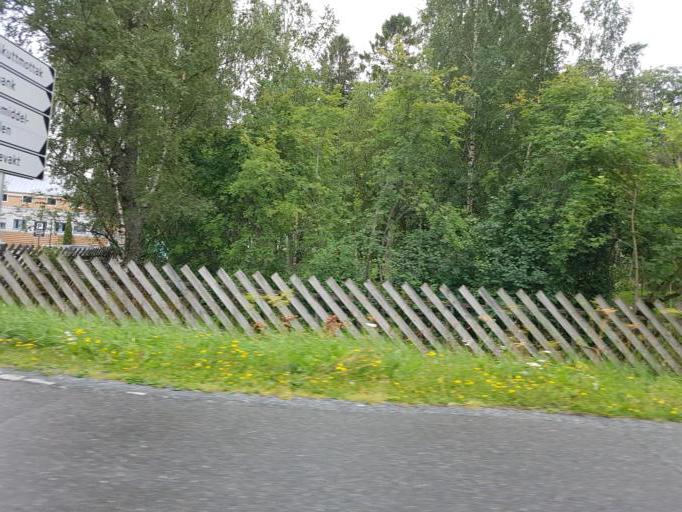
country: NO
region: Nord-Trondelag
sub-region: Levanger
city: Levanger
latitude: 63.7415
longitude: 11.2855
